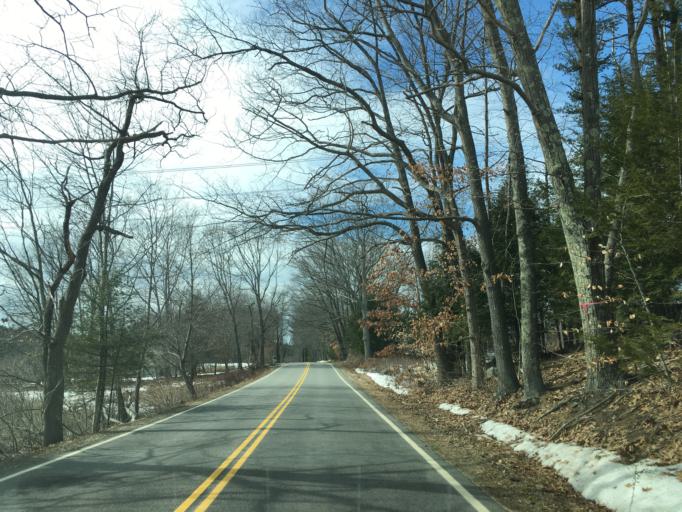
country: US
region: New Hampshire
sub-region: Rockingham County
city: North Hampton
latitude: 42.9957
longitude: -70.8541
